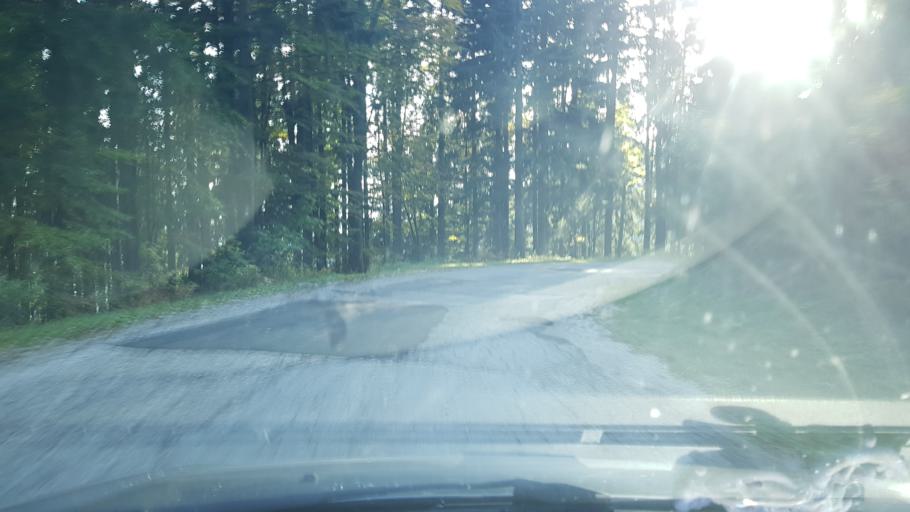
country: SI
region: Slovenj Gradec
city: Legen
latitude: 46.4919
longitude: 15.1836
